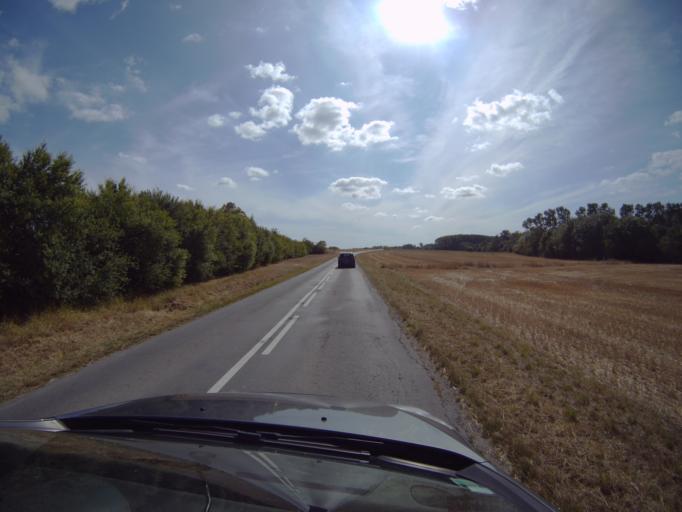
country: FR
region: Poitou-Charentes
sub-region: Departement des Deux-Sevres
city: Saint-Hilaire-la-Palud
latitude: 46.2598
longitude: -0.7296
